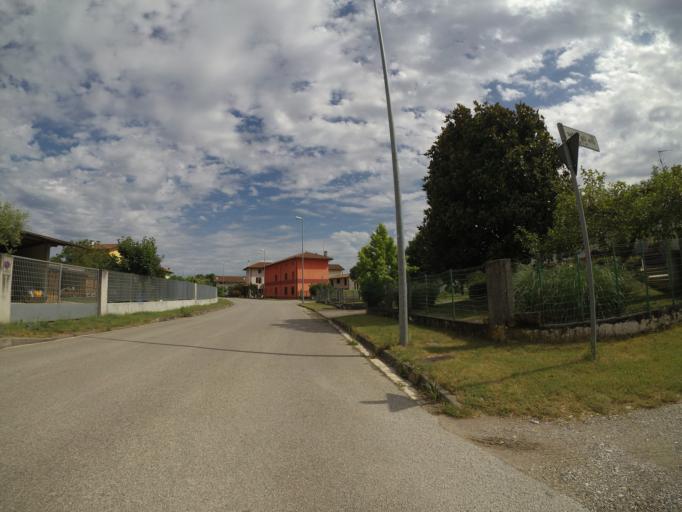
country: IT
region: Friuli Venezia Giulia
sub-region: Provincia di Udine
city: Lestizza
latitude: 45.9658
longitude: 13.1172
